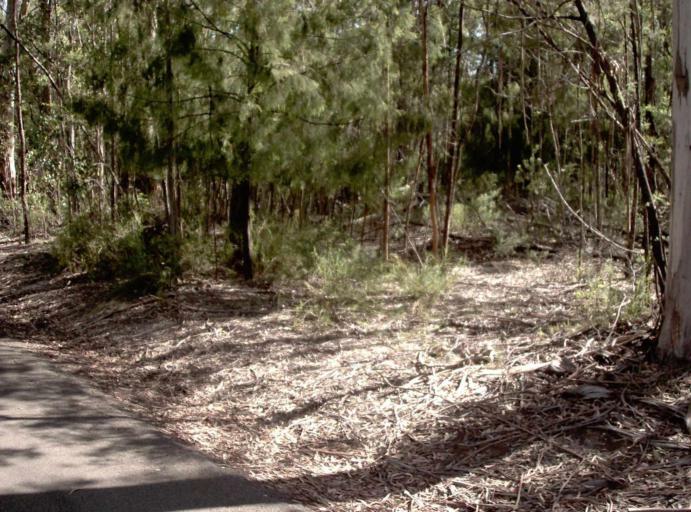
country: AU
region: Victoria
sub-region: East Gippsland
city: Lakes Entrance
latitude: -37.4724
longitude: 148.1239
